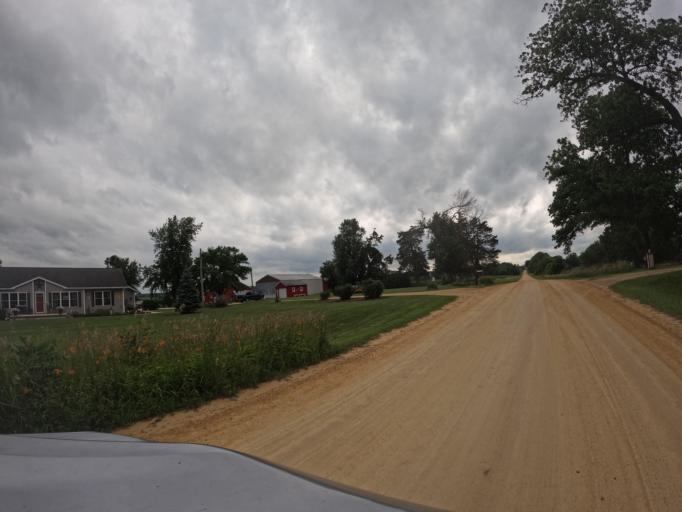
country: US
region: Iowa
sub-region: Clinton County
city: De Witt
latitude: 41.7987
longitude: -90.5517
